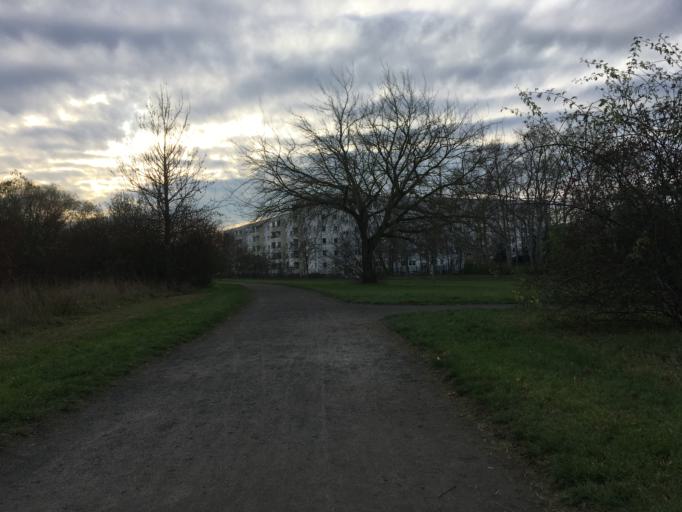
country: DE
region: Berlin
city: Falkenberg
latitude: 52.5672
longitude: 13.5345
